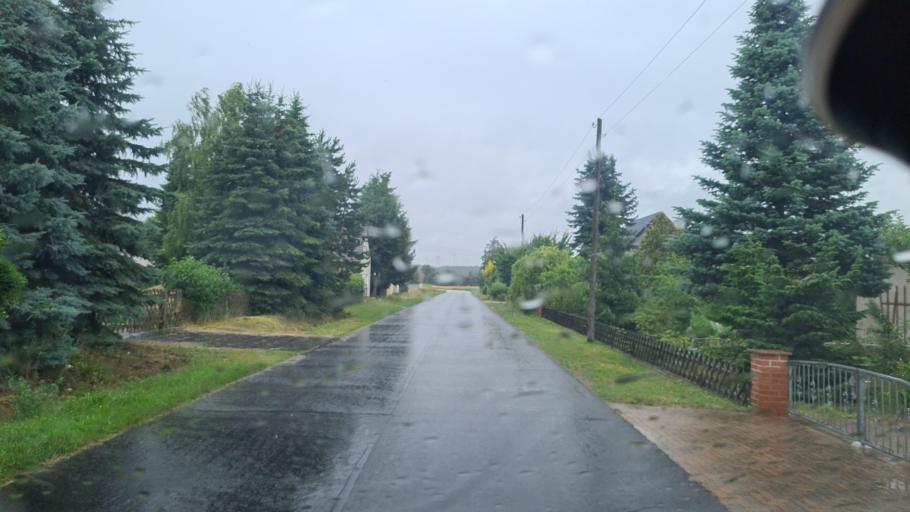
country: DE
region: Brandenburg
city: Juterbog
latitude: 51.9787
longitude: 13.1715
